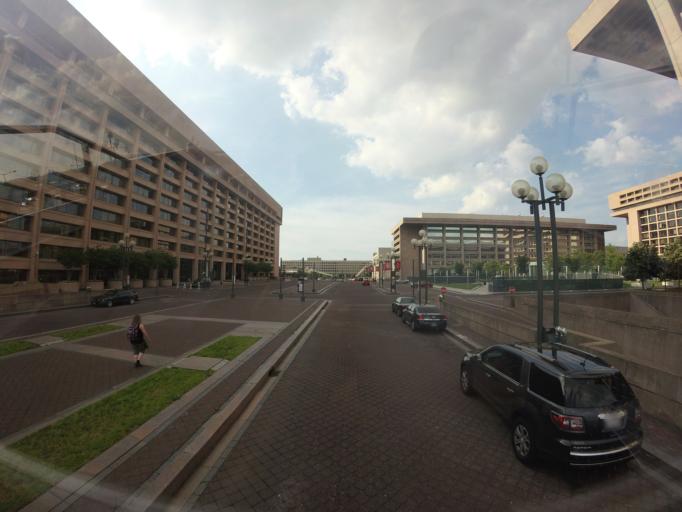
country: US
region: Washington, D.C.
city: Washington, D.C.
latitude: 38.8833
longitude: -77.0260
